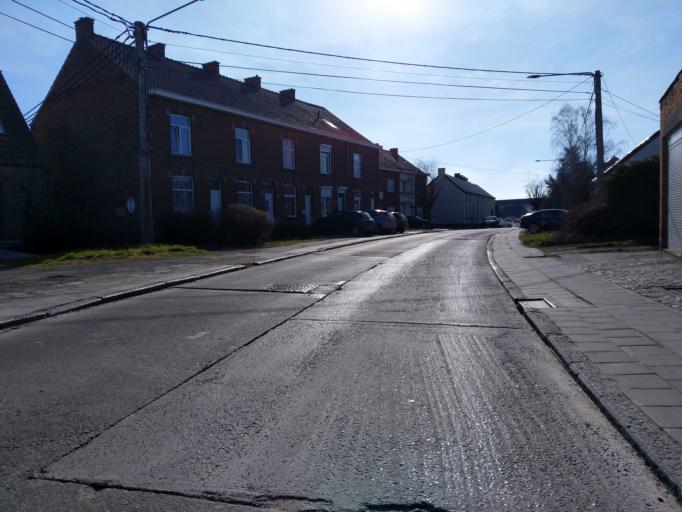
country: BE
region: Wallonia
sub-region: Province du Hainaut
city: Quevy-le-Petit
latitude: 50.3418
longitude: 3.9031
